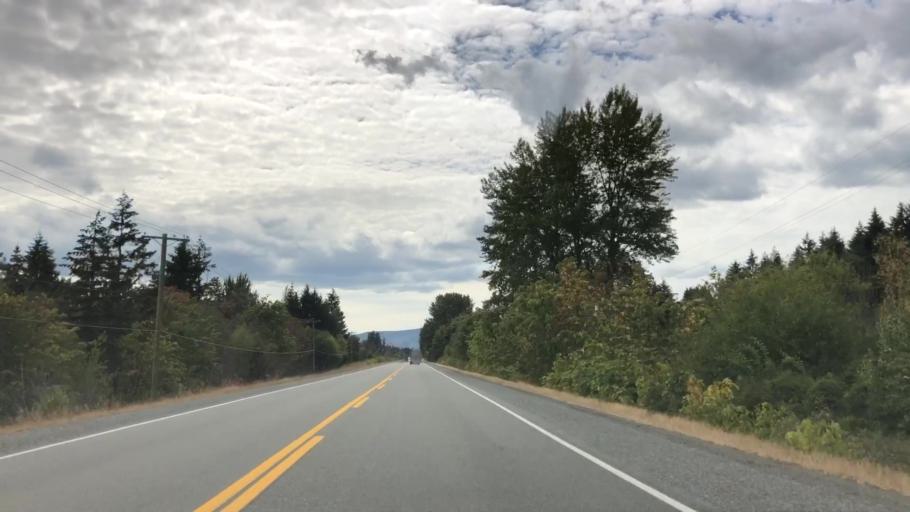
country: CA
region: British Columbia
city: Duncan
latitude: 48.8103
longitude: -123.7508
